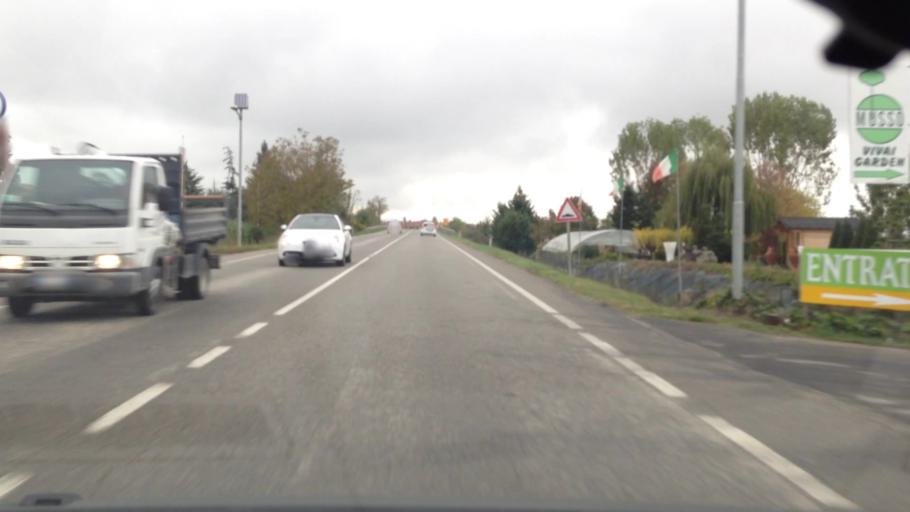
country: IT
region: Piedmont
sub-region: Provincia di Torino
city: Riva Presso Chieri
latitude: 44.9829
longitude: 7.8783
